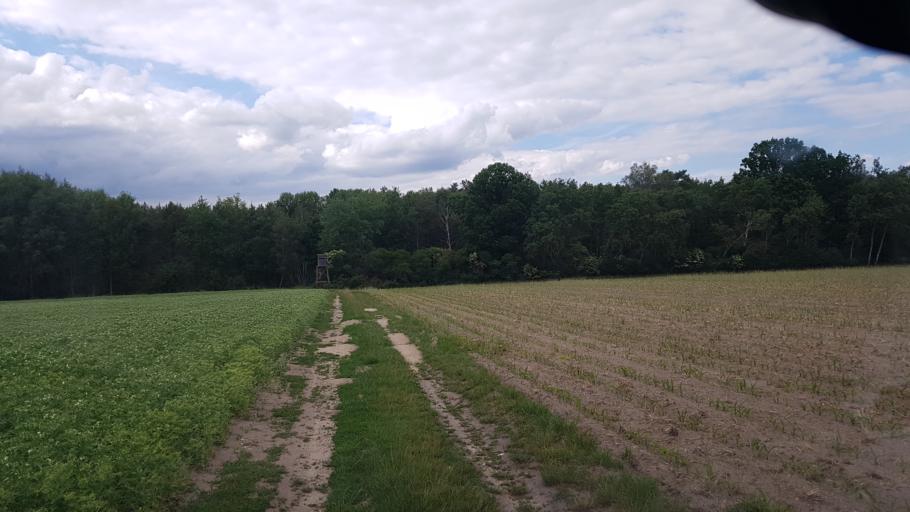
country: DE
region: Brandenburg
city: Finsterwalde
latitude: 51.6166
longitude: 13.6603
